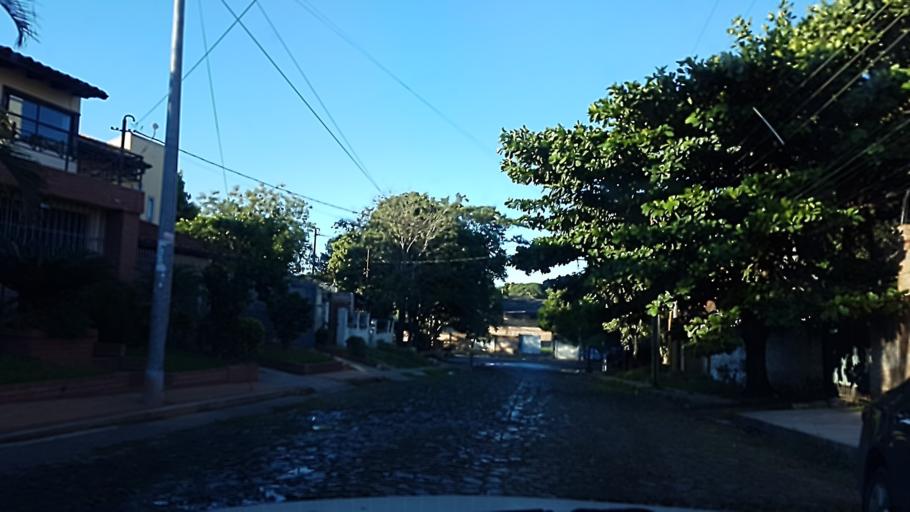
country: PY
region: Asuncion
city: Asuncion
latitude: -25.2738
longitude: -57.5683
